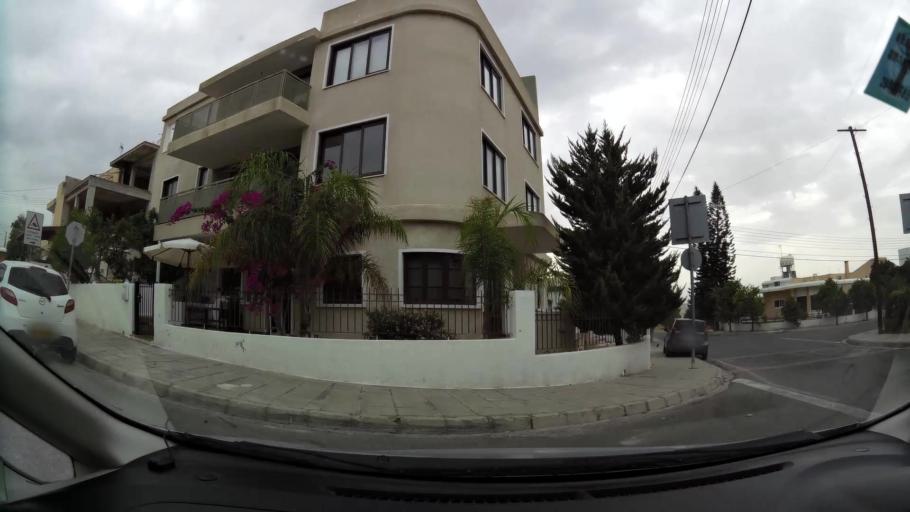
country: CY
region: Lefkosia
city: Geri
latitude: 35.1129
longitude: 33.3796
